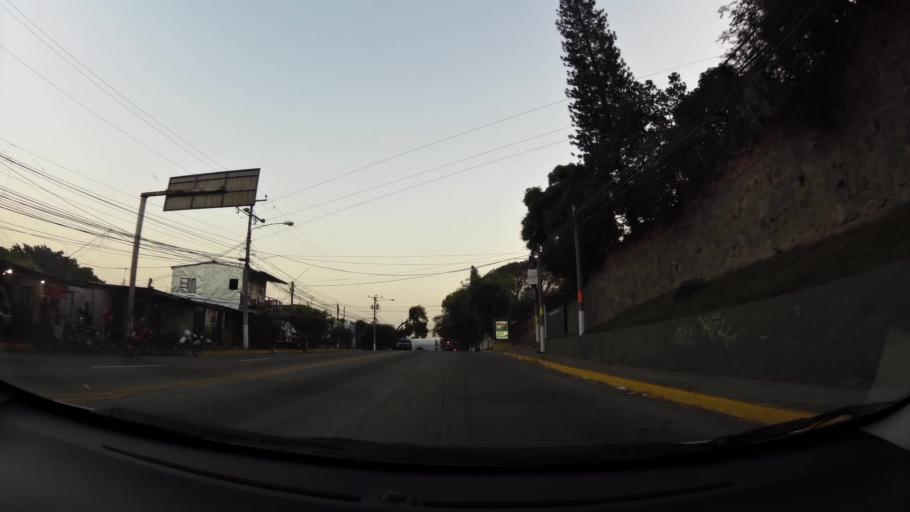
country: SV
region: San Salvador
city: Mejicanos
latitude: 13.7052
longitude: -89.2264
